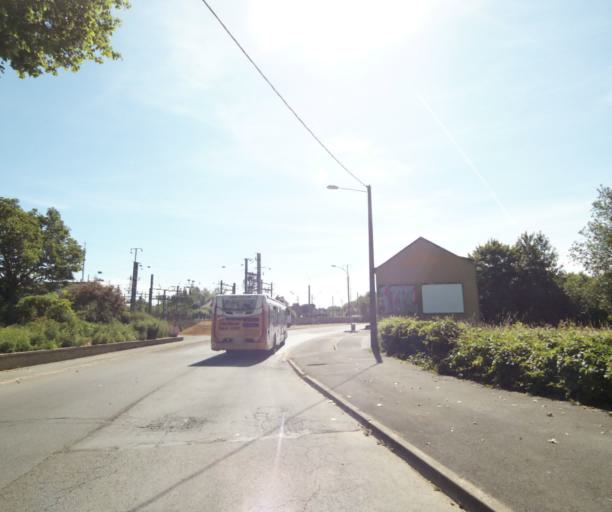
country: FR
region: Champagne-Ardenne
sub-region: Departement des Ardennes
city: Villers-Semeuse
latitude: 49.7518
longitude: 4.7340
